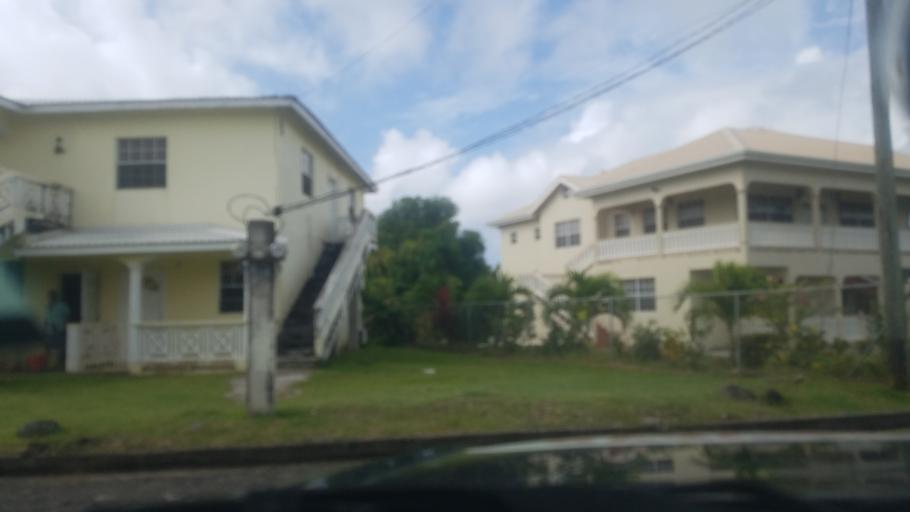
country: LC
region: Laborie Quarter
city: Laborie
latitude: 13.7487
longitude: -60.9762
